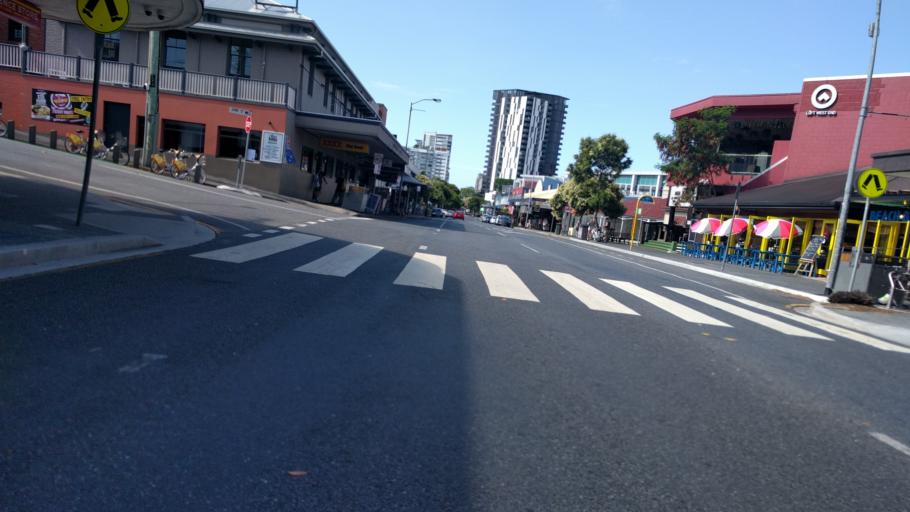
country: AU
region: Queensland
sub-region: Brisbane
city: South Brisbane
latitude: -27.4793
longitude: 153.0123
